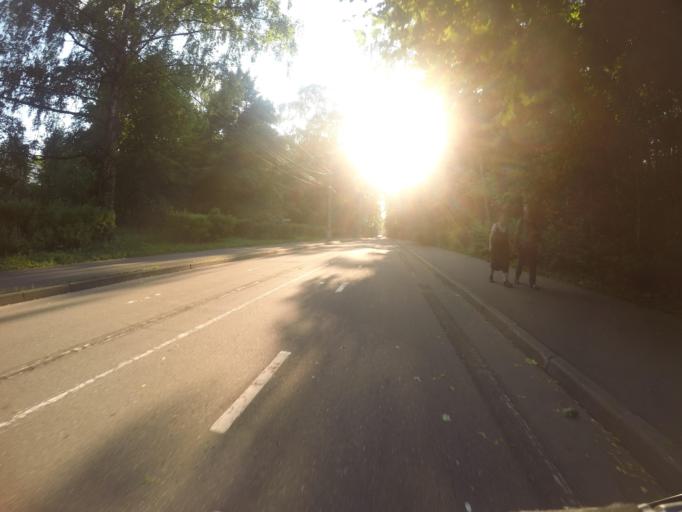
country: RU
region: Moscow
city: Sokol'niki
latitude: 55.7968
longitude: 37.6633
